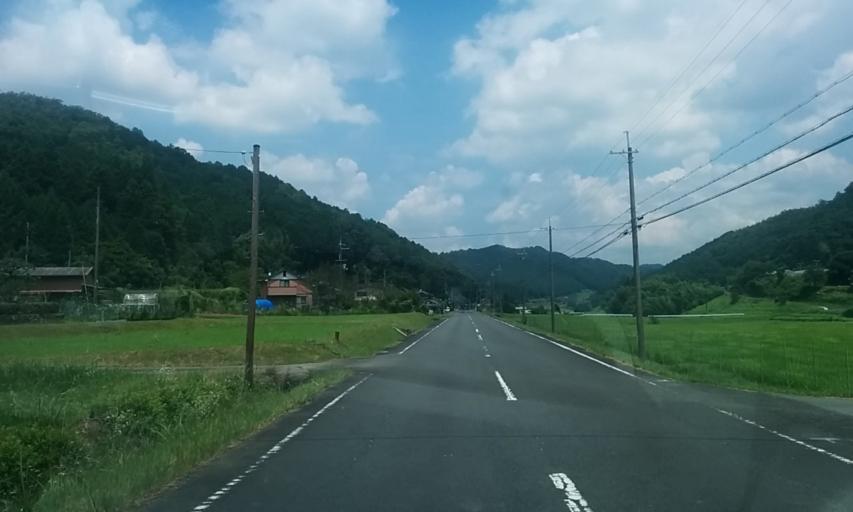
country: JP
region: Kyoto
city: Ayabe
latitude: 35.2012
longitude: 135.2225
